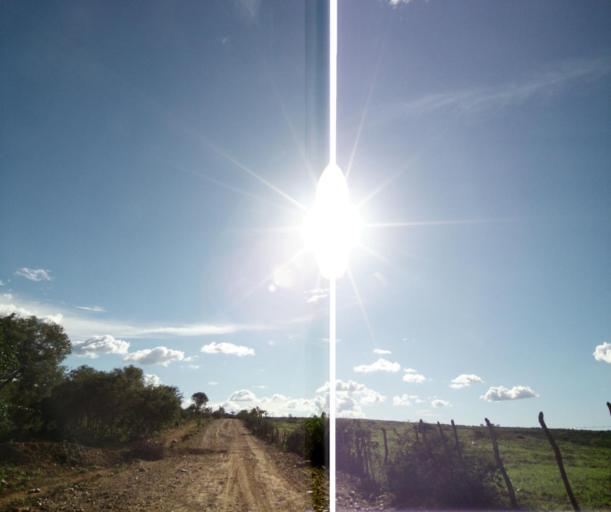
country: BR
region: Bahia
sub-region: Tanhacu
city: Tanhacu
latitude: -14.1832
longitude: -40.9327
